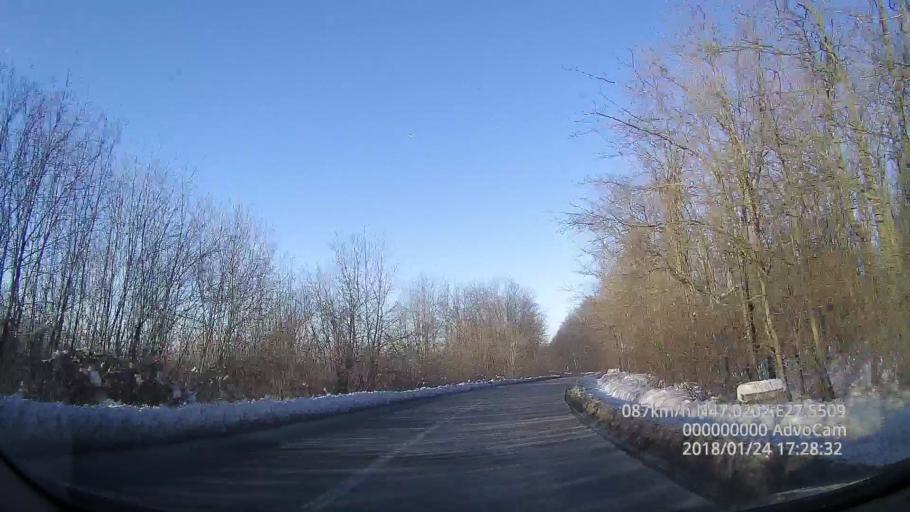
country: RO
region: Iasi
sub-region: Comuna Mogosesti
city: Mogosesti
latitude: 47.0210
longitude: 27.5507
